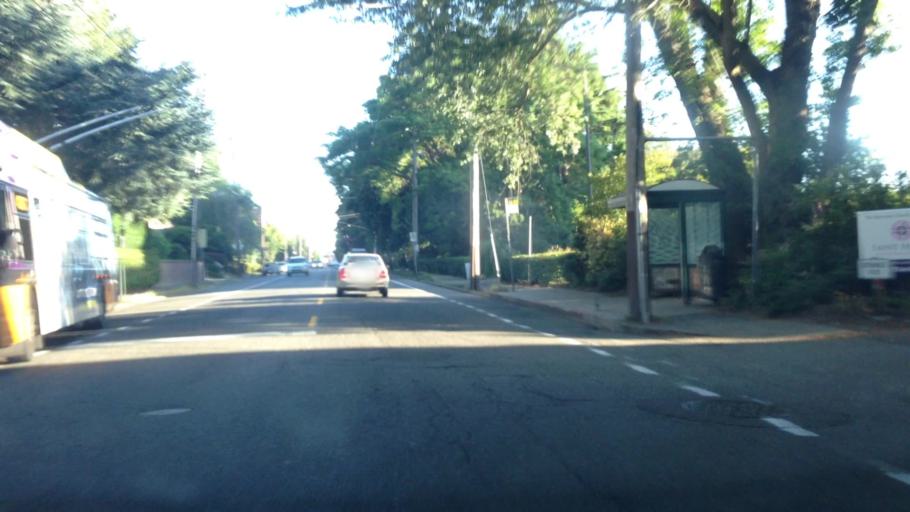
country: US
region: Washington
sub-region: King County
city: Seattle
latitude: 47.6323
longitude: -122.3203
